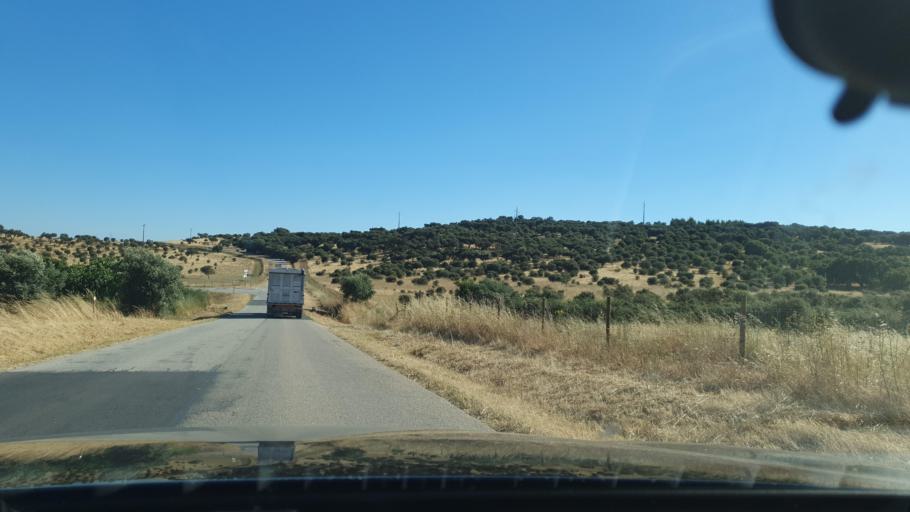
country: PT
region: Evora
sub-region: Alandroal
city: Alandroal
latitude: 38.7341
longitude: -7.4038
